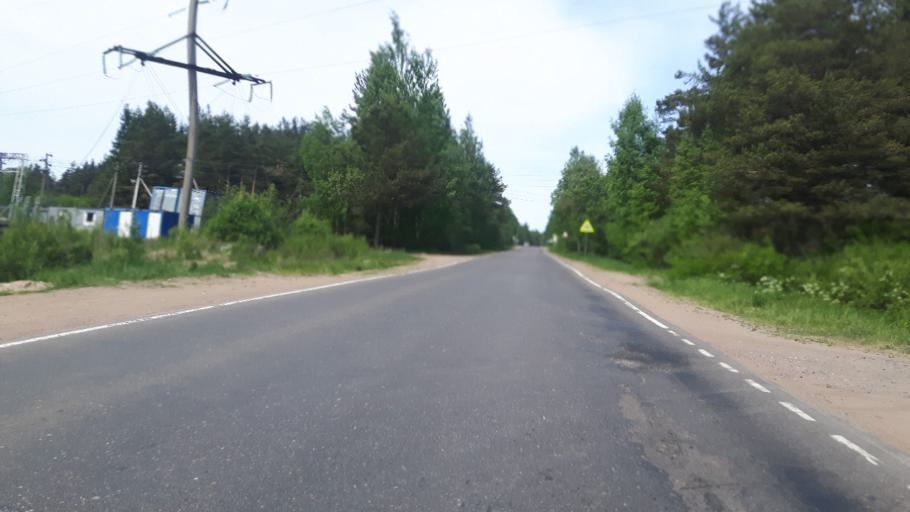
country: RU
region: Leningrad
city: Ust'-Luga
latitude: 59.6435
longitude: 28.2720
